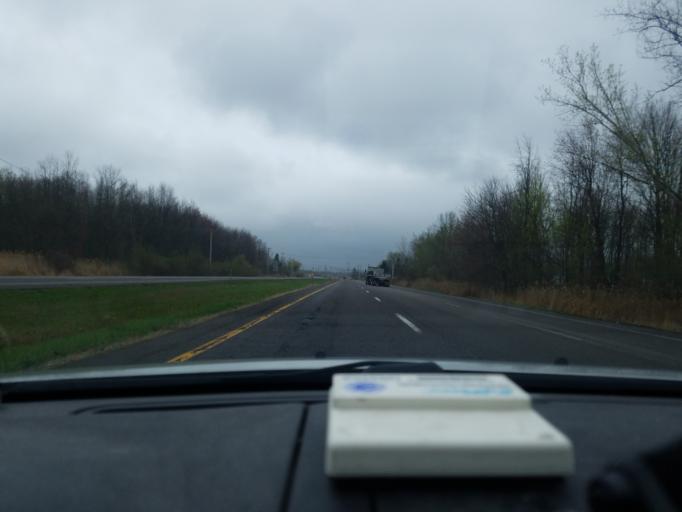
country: US
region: New York
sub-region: Onondaga County
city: North Syracuse
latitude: 43.1344
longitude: -76.0823
